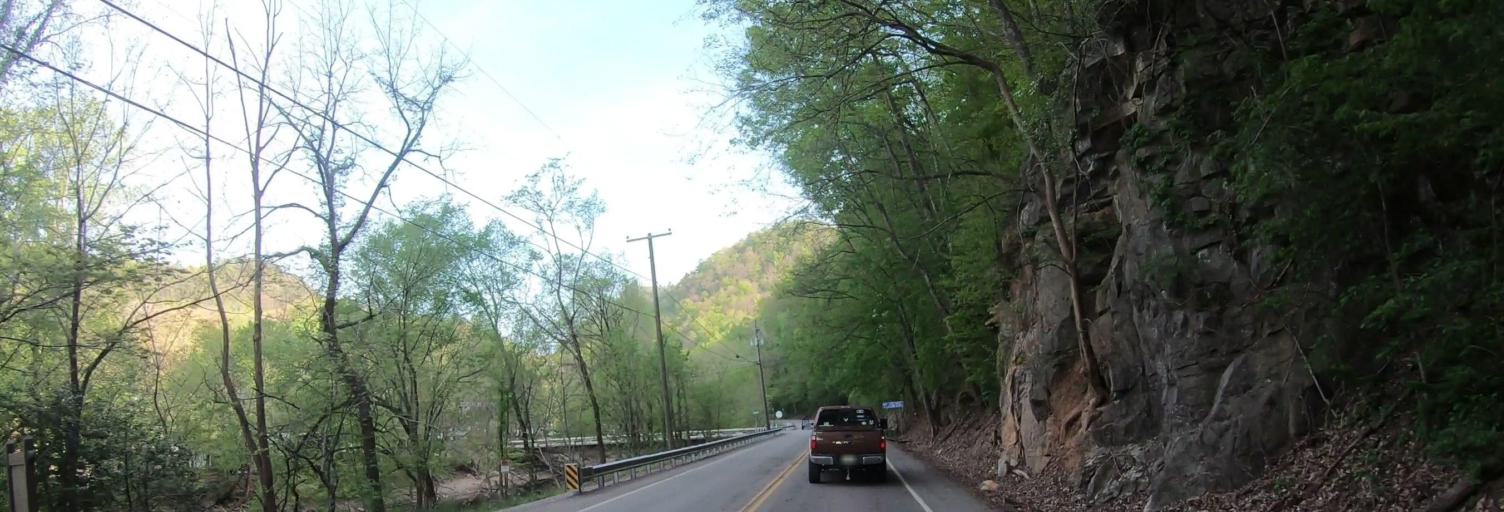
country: US
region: Tennessee
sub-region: Sevier County
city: Pigeon Forge
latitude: 35.6715
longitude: -83.7176
